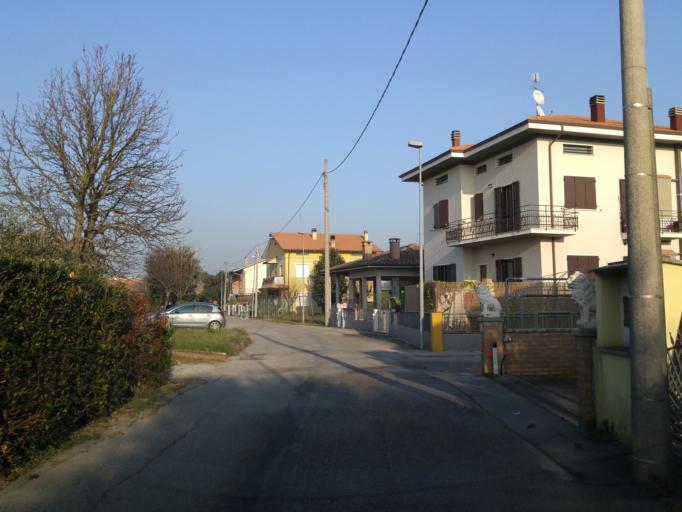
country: IT
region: The Marches
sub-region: Provincia di Pesaro e Urbino
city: Lucrezia
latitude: 43.7707
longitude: 12.9471
